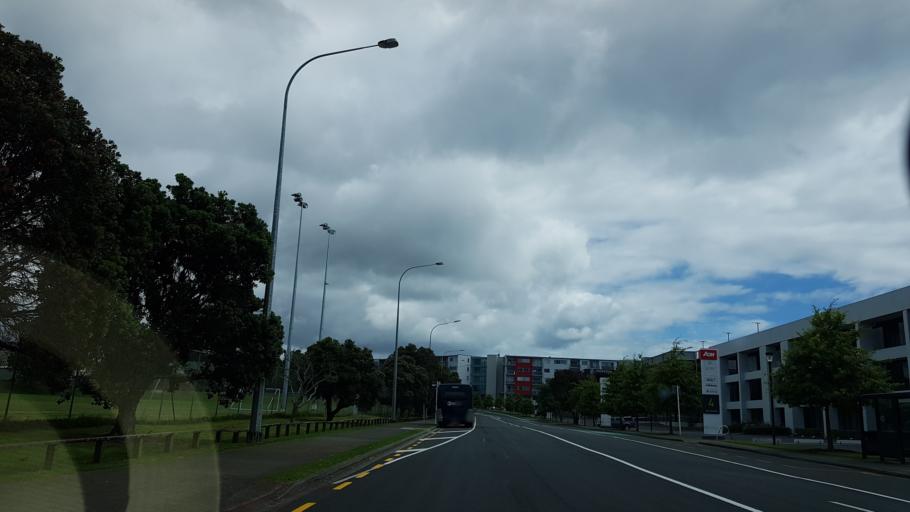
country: NZ
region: Auckland
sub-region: Auckland
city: North Shore
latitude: -36.7930
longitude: 174.7632
